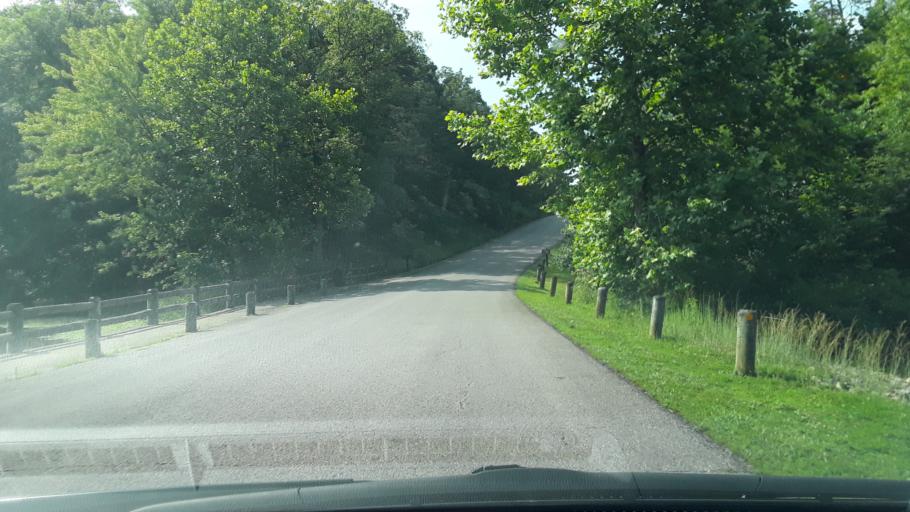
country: US
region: Indiana
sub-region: Clark County
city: Henryville
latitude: 38.4644
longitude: -85.8655
